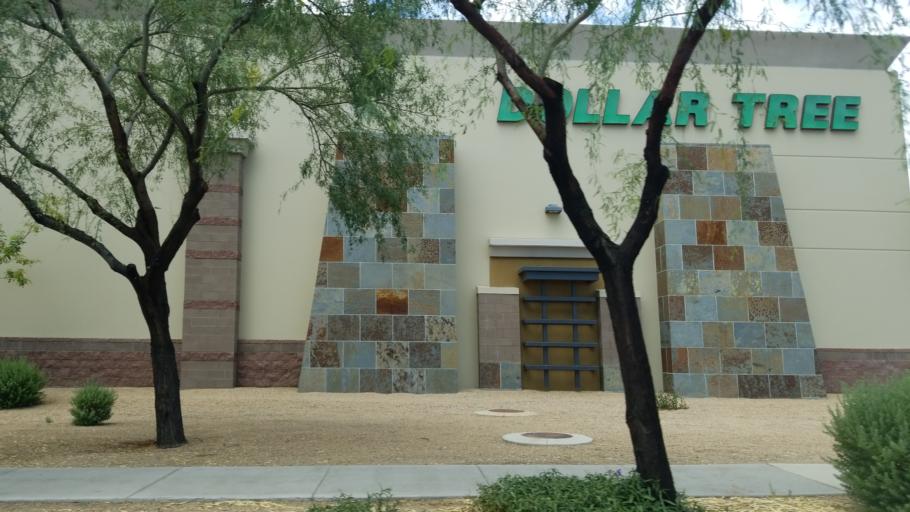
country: US
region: Arizona
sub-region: Maricopa County
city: Anthem
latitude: 33.7087
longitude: -112.1089
